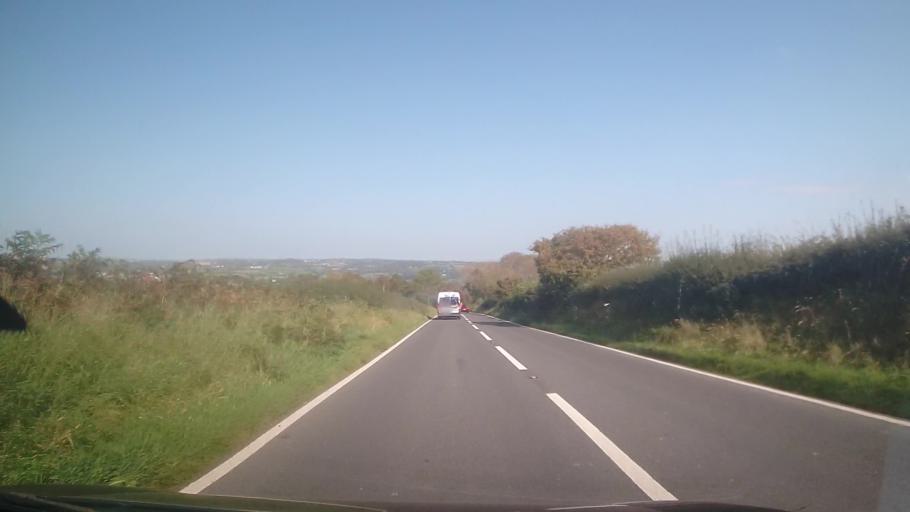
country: GB
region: Wales
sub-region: County of Ceredigion
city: Cardigan
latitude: 52.0703
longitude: -4.6646
